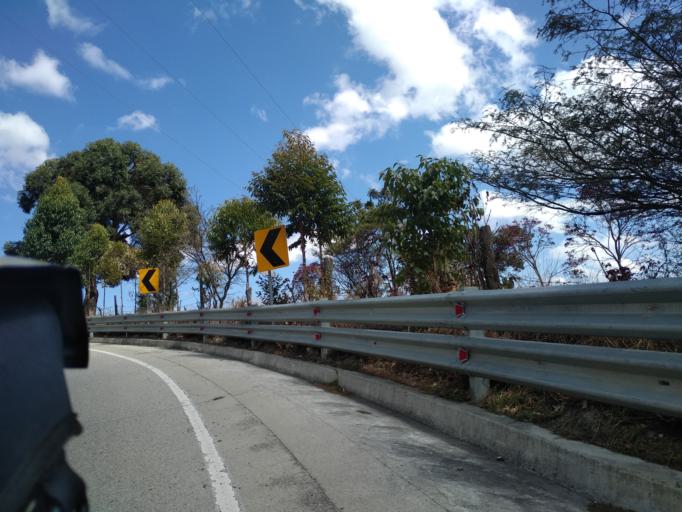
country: EC
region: Loja
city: Loja
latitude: -4.3463
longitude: -79.1908
